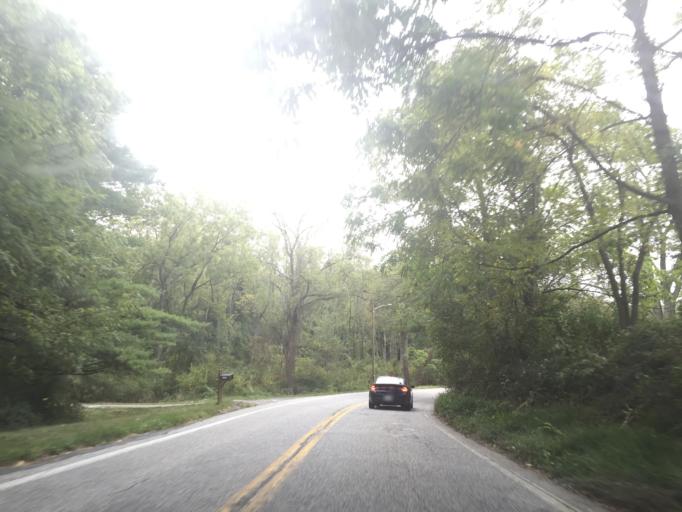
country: US
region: Maryland
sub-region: Baltimore County
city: Carney
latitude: 39.4463
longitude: -76.5074
